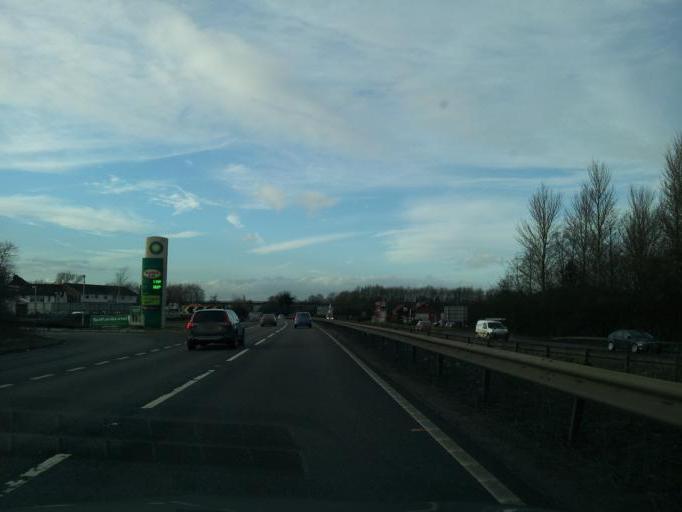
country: GB
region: England
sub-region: Peterborough
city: Castor
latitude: 52.5436
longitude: -0.3301
